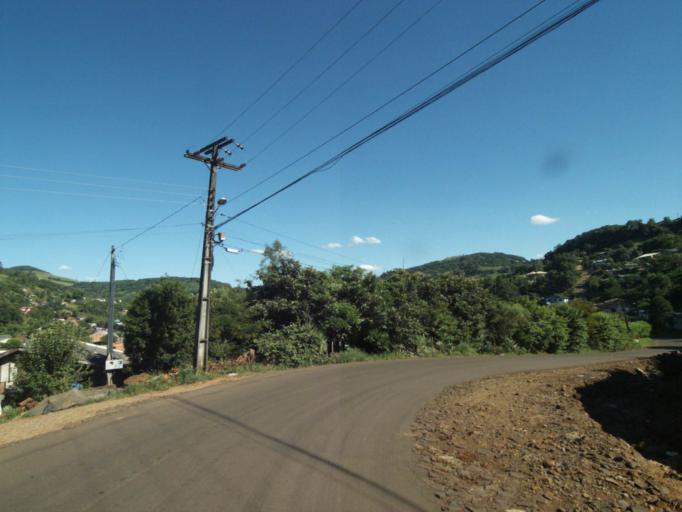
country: BR
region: Parana
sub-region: Ampere
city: Ampere
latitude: -26.1696
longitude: -53.3659
